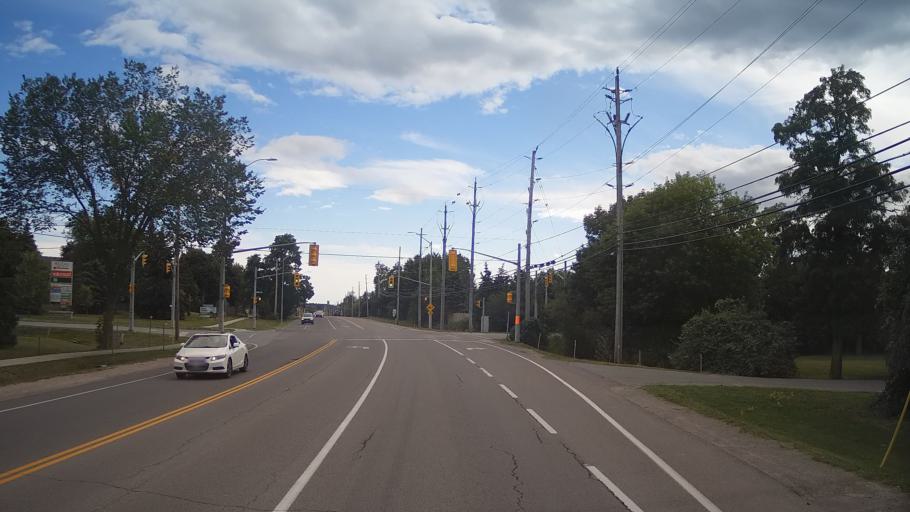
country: CA
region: Ontario
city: Kingston
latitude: 44.2599
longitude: -76.4603
